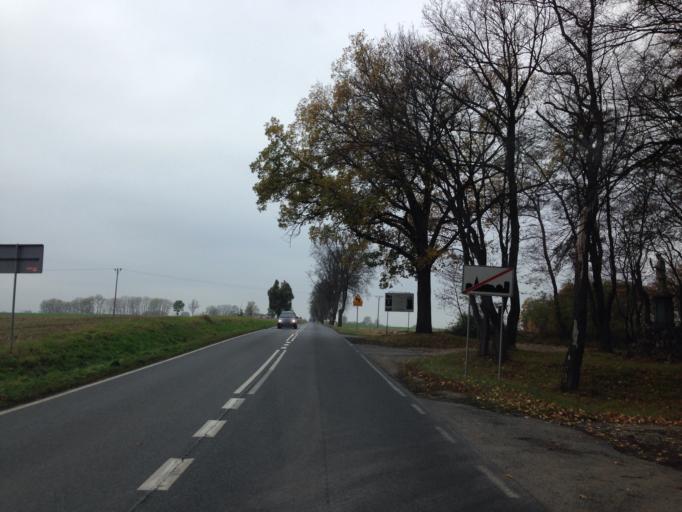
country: PL
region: Kujawsko-Pomorskie
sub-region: Powiat brodnicki
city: Jablonowo Pomorskie
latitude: 53.3862
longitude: 19.1335
